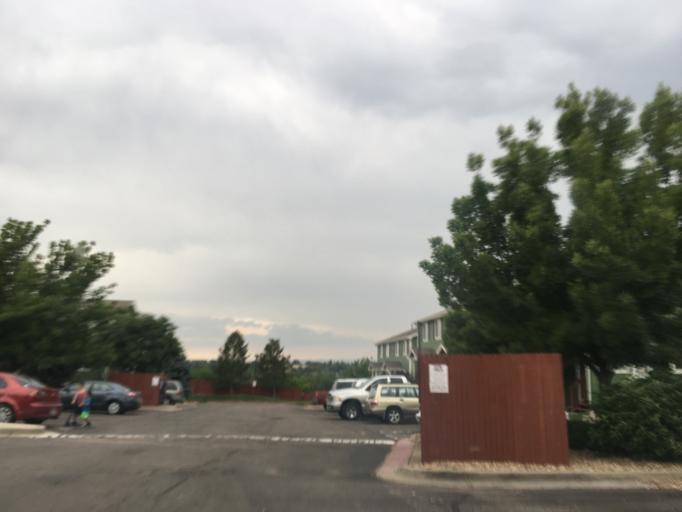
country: US
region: Colorado
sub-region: Arapahoe County
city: Sheridan
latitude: 39.6551
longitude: -105.0284
